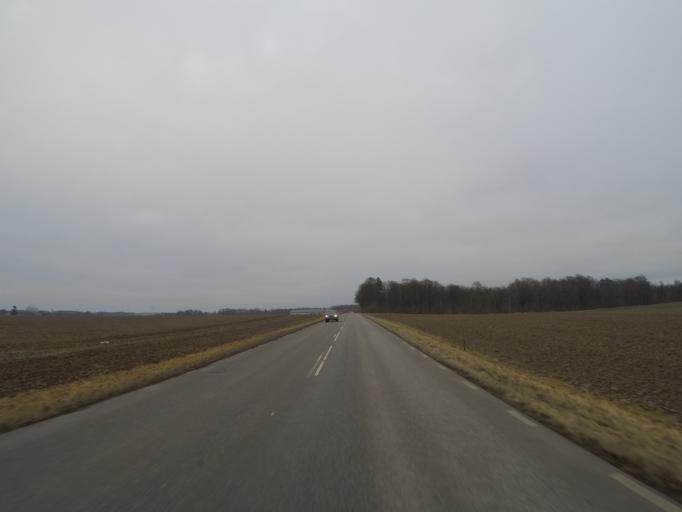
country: SE
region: Skane
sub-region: Hoors Kommun
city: Loberod
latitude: 55.7729
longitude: 13.4920
